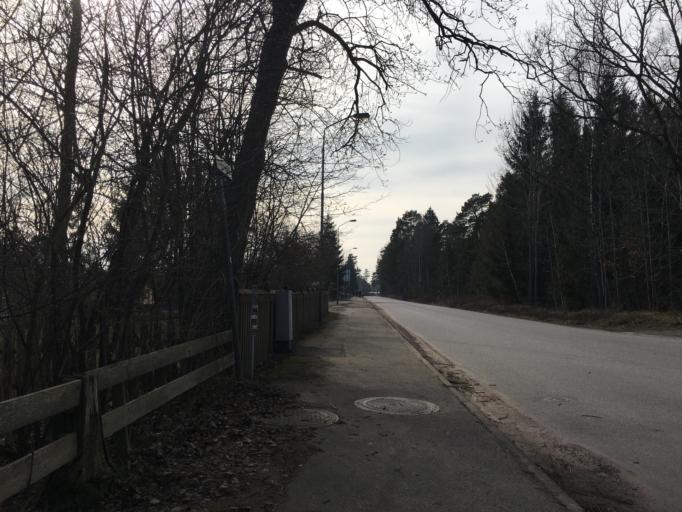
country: SE
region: Kalmar
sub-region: Kalmar Kommun
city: Kalmar
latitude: 56.7004
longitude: 16.3678
